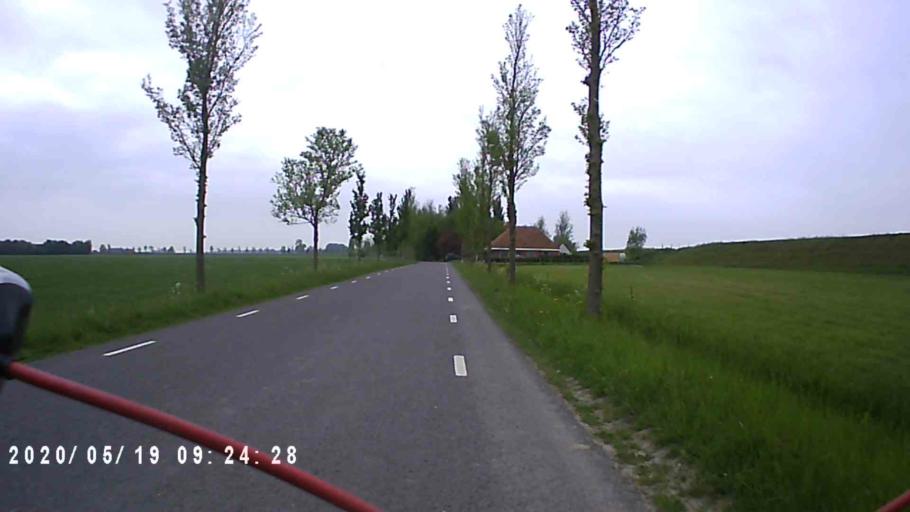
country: NL
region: Groningen
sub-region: Gemeente Zuidhorn
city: Grijpskerk
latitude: 53.2943
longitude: 6.3387
